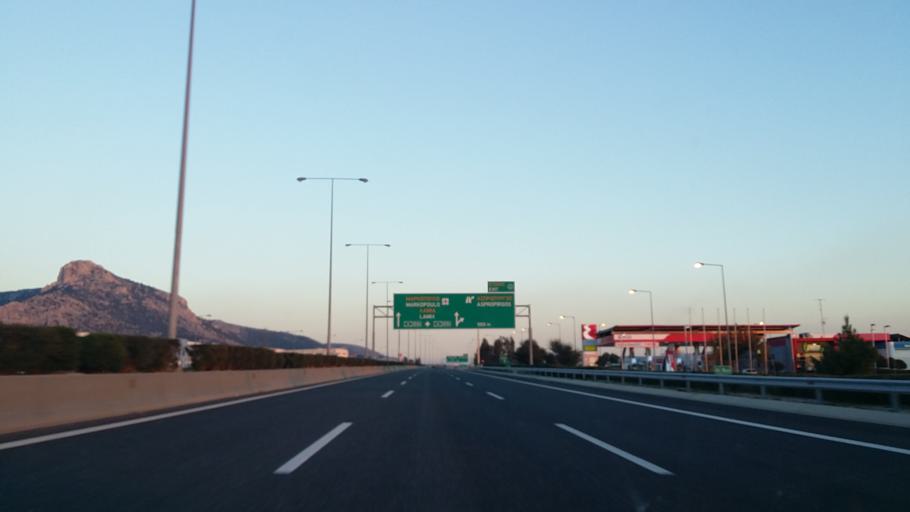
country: GR
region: Attica
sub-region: Nomarchia Dytikis Attikis
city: Aspropyrgos
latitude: 38.0930
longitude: 23.6046
